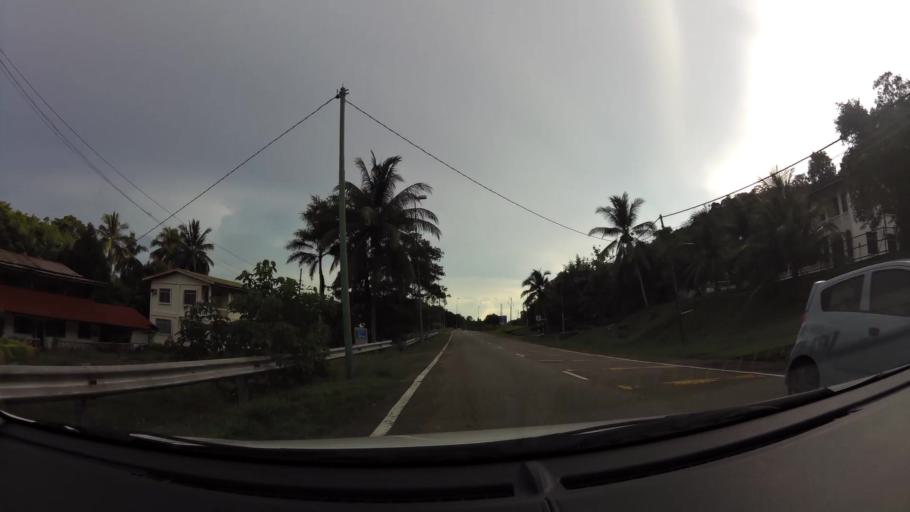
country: BN
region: Brunei and Muara
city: Bandar Seri Begawan
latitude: 4.9148
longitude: 115.0039
